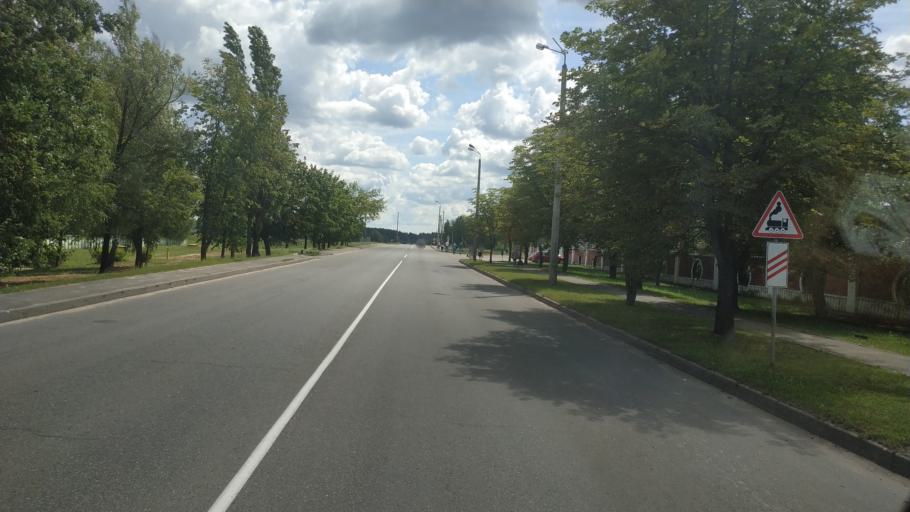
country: BY
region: Mogilev
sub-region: Mahilyowski Rayon
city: Veyno
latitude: 53.8406
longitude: 30.3942
